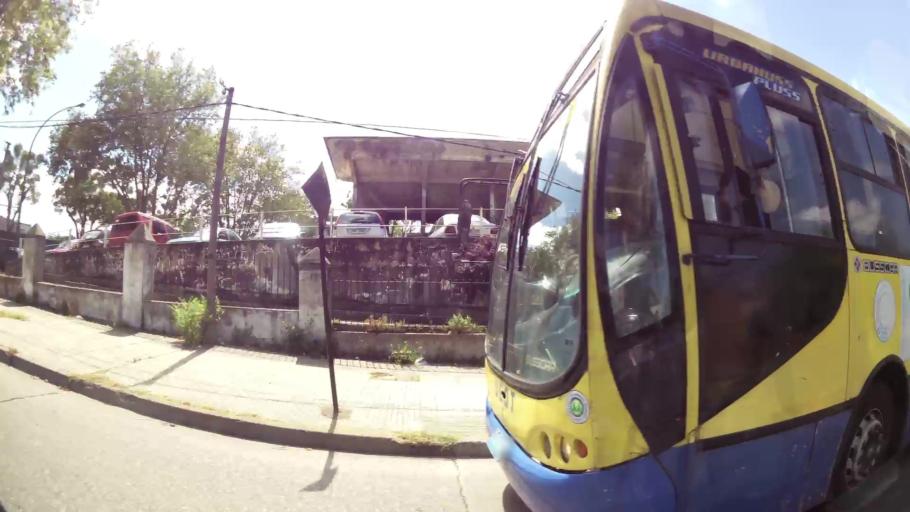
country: UY
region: Montevideo
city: Montevideo
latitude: -34.8568
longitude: -56.1440
